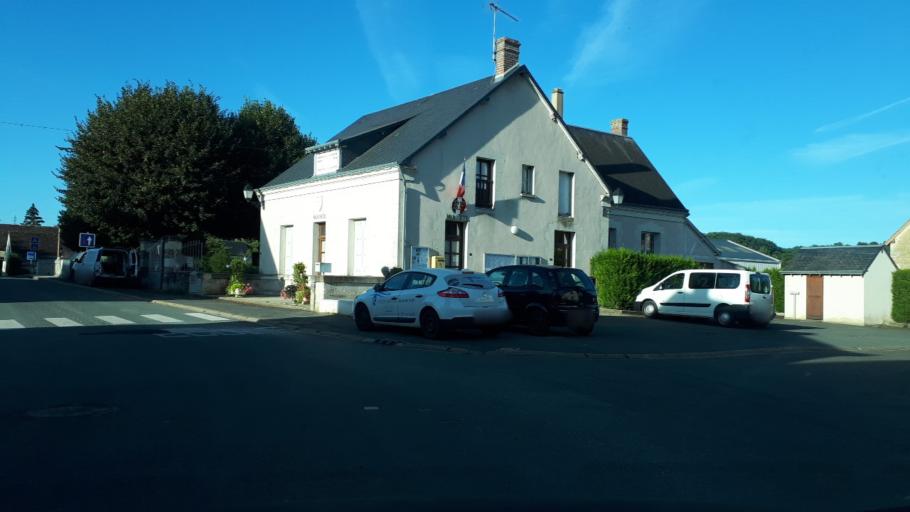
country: FR
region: Centre
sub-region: Departement du Loir-et-Cher
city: Lunay
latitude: 47.7516
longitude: 0.9380
